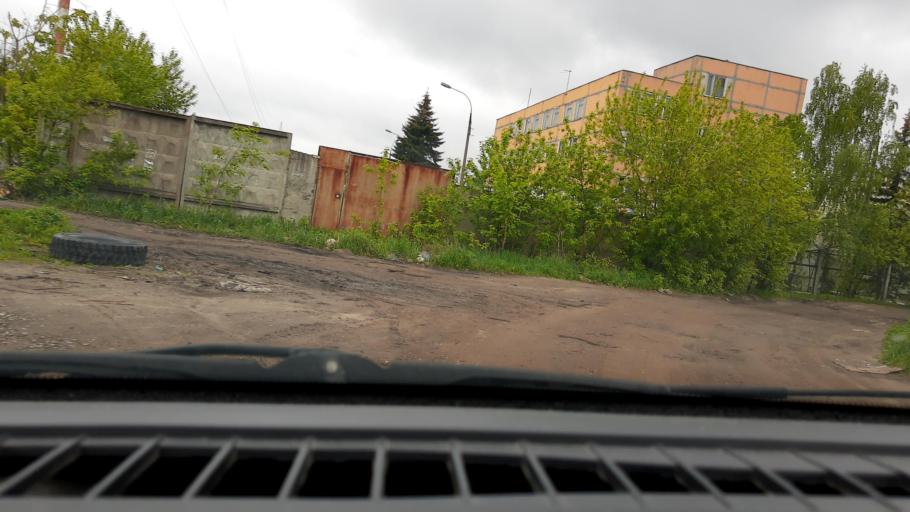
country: RU
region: Nizjnij Novgorod
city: Nizhniy Novgorod
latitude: 56.2718
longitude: 43.8980
